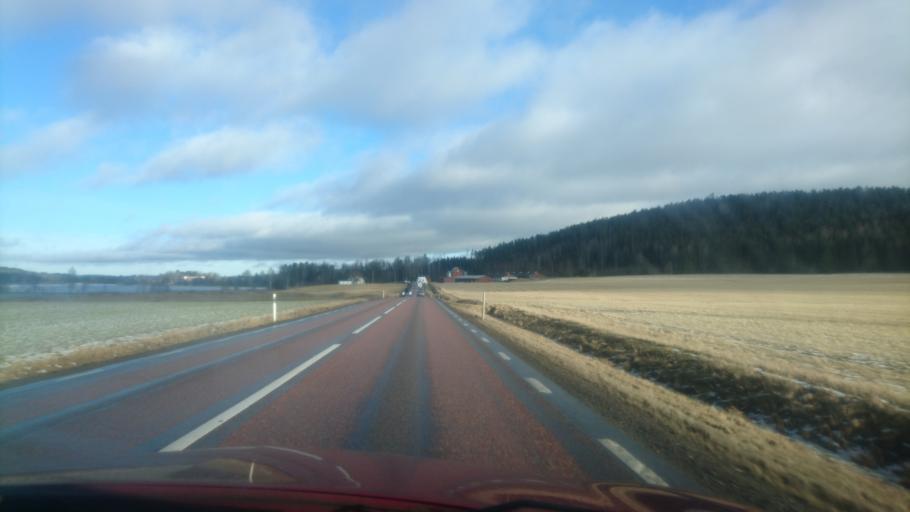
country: SE
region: Vaermland
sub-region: Karlstads Kommun
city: Edsvalla
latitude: 59.6234
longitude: 13.1595
